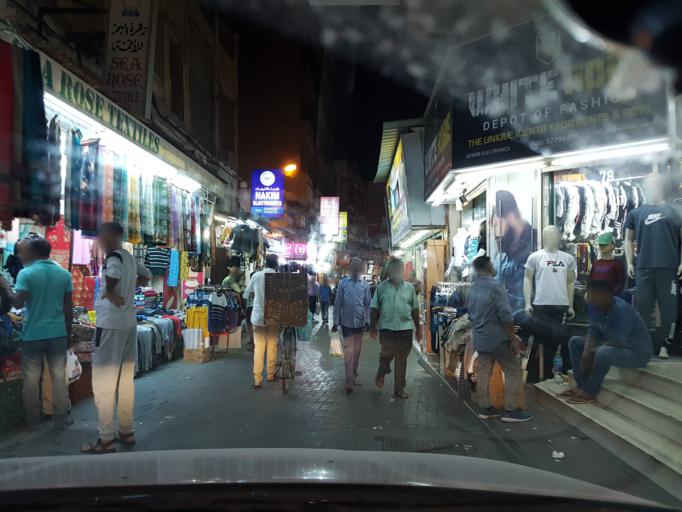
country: BH
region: Manama
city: Manama
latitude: 26.2320
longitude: 50.5759
